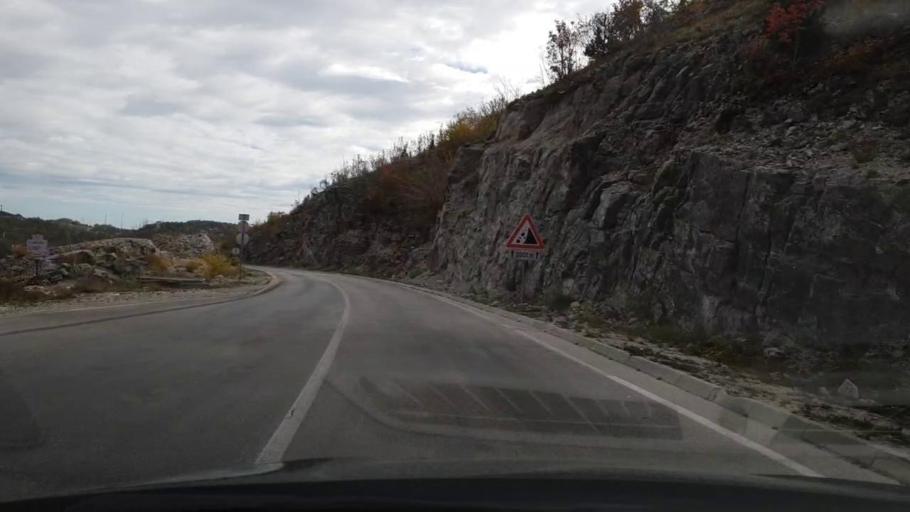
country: ME
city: Igalo
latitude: 42.5609
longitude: 18.4441
